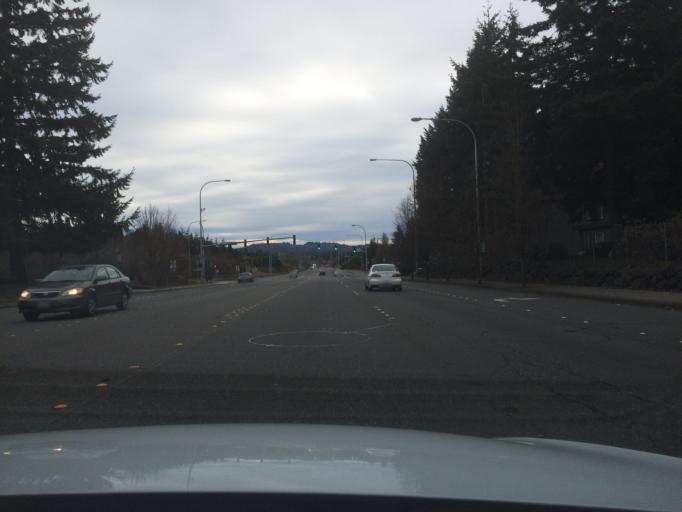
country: US
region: Washington
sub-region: King County
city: Redmond
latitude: 47.6376
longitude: -122.1431
